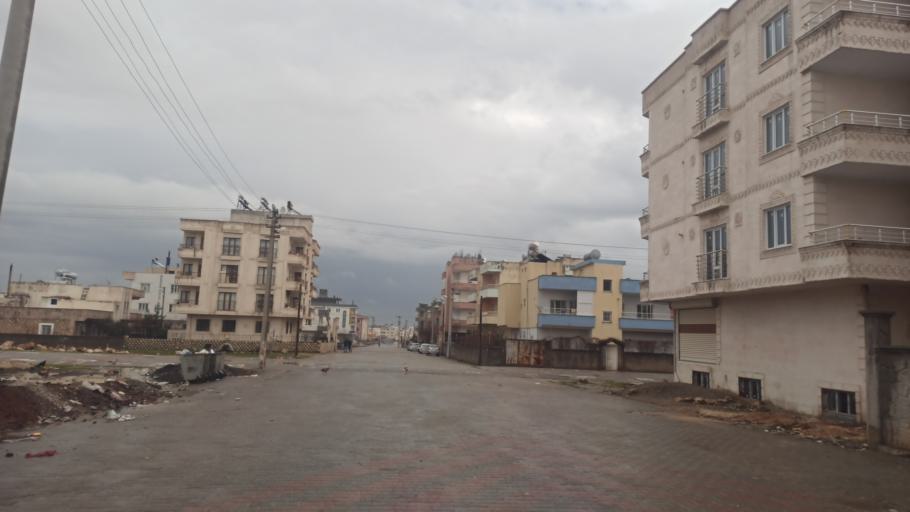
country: TR
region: Mardin
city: Midyat
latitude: 37.4237
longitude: 41.3544
